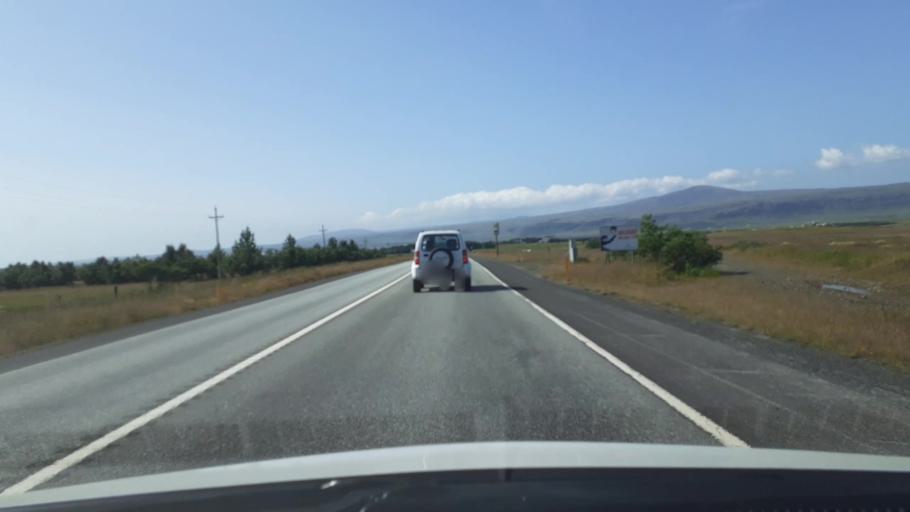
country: IS
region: South
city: Hveragerdi
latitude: 63.9587
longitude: -21.1060
